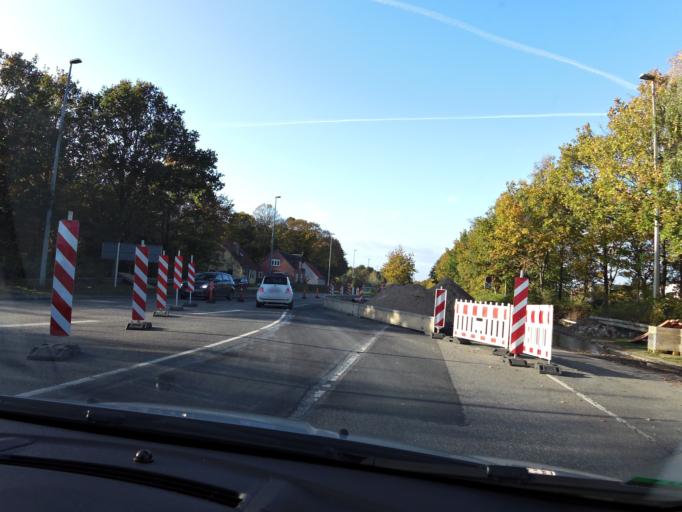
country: DK
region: South Denmark
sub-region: Odense Kommune
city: Neder Holluf
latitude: 55.3725
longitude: 10.4443
